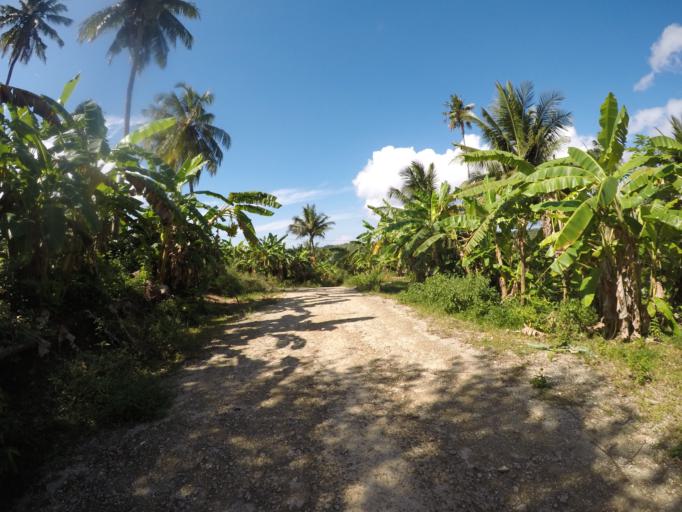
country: TZ
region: Pemba South
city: Mtambile
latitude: -5.3468
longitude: 39.6903
